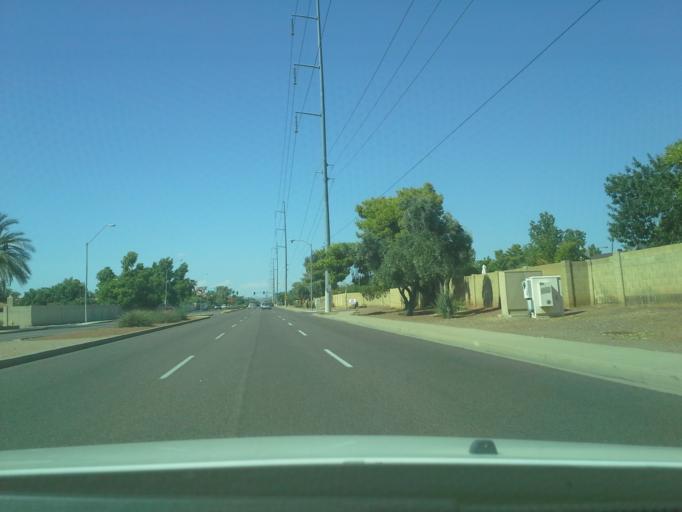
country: US
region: Arizona
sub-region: Maricopa County
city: Glendale
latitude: 33.6305
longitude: -112.0654
